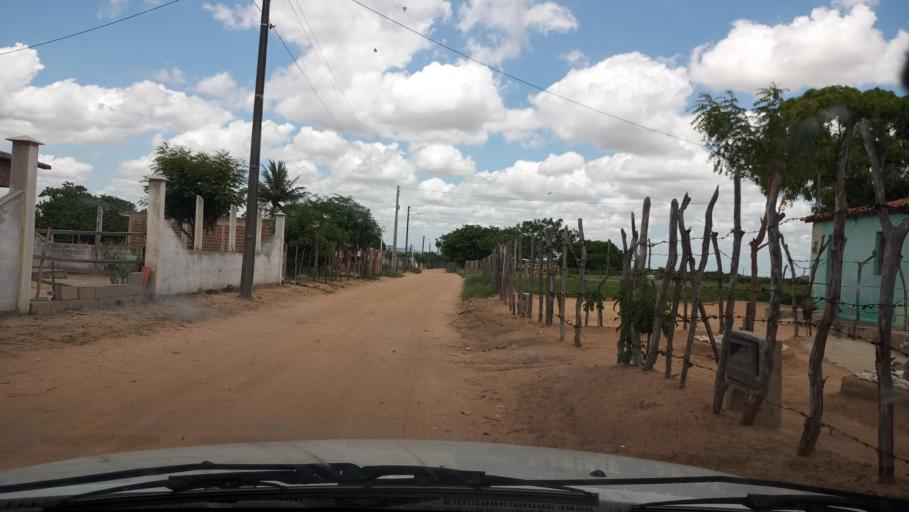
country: BR
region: Rio Grande do Norte
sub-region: Sao Jose Do Campestre
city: Sao Jose do Campestre
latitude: -6.4332
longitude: -35.6349
